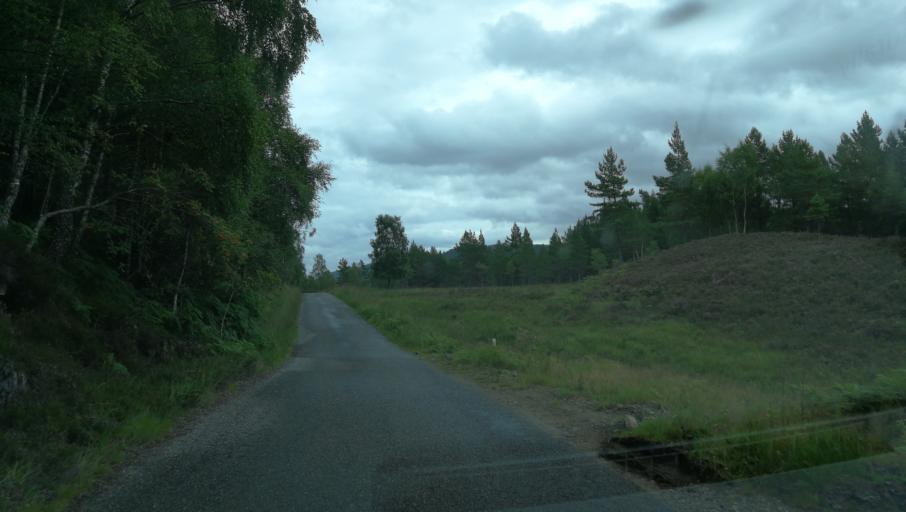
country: GB
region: Scotland
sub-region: Highland
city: Spean Bridge
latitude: 57.2787
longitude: -4.9415
